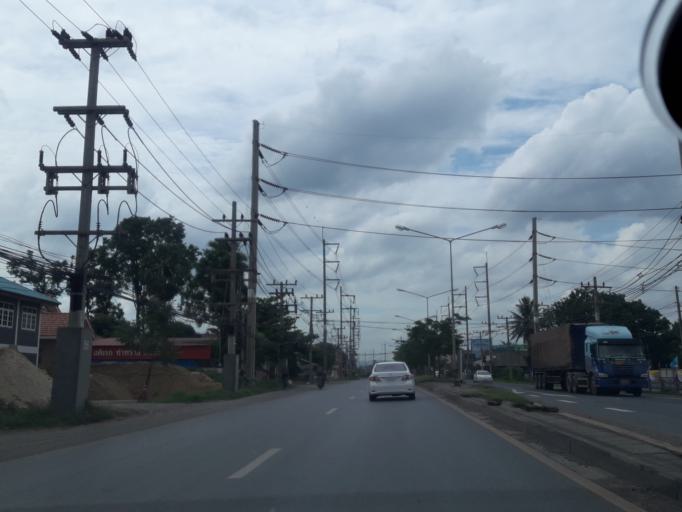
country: TH
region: Sara Buri
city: Kaeng Khoi
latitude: 14.5662
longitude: 101.0069
